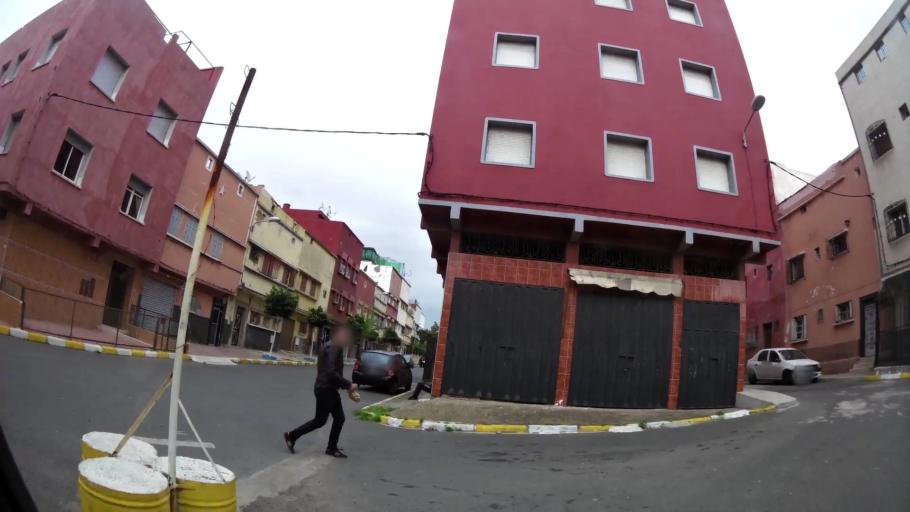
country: MA
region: Grand Casablanca
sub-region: Casablanca
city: Casablanca
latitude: 33.5664
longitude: -7.5592
